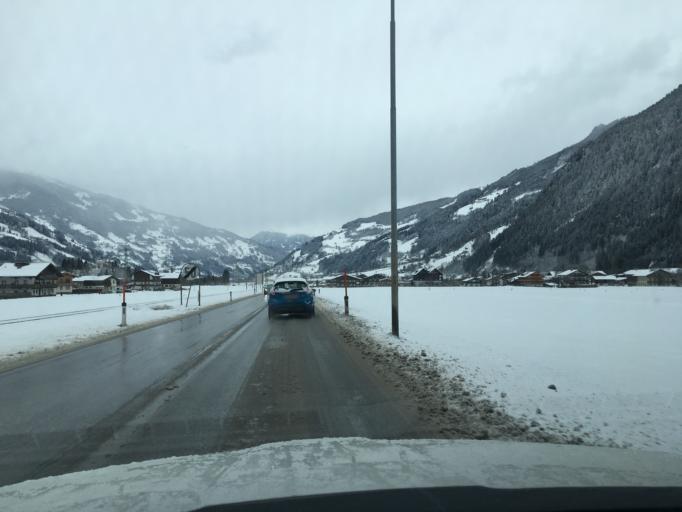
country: AT
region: Tyrol
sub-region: Politischer Bezirk Schwaz
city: Mayrhofen
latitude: 47.1718
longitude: 11.8644
